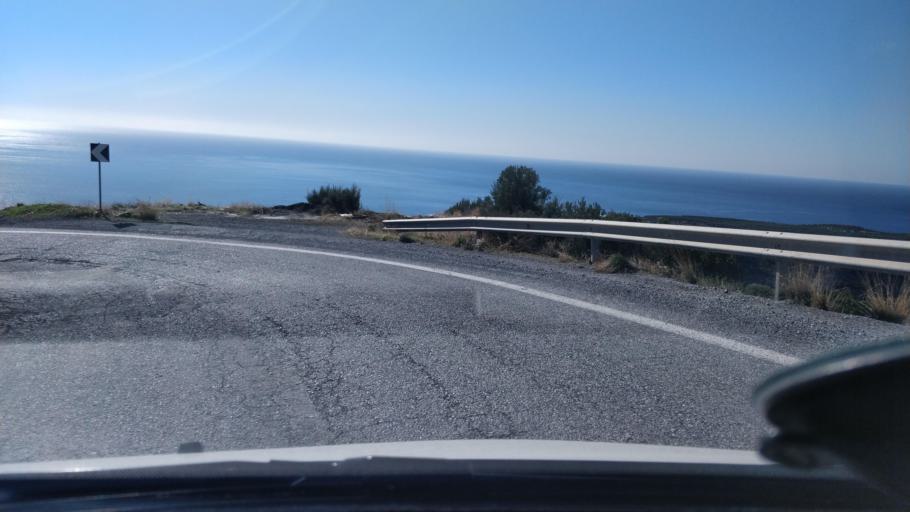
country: GR
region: Crete
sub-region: Nomos Irakleiou
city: Arkalochori
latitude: 35.0065
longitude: 25.4330
